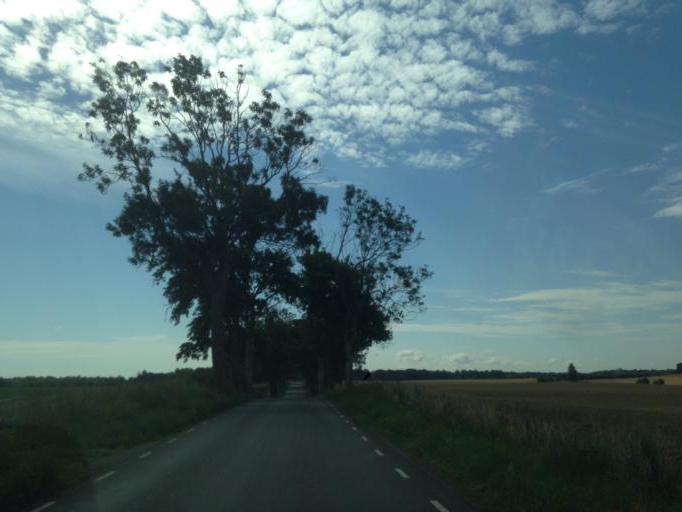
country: SE
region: Skane
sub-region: Tomelilla Kommun
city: Tomelilla
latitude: 55.6507
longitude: 14.0342
